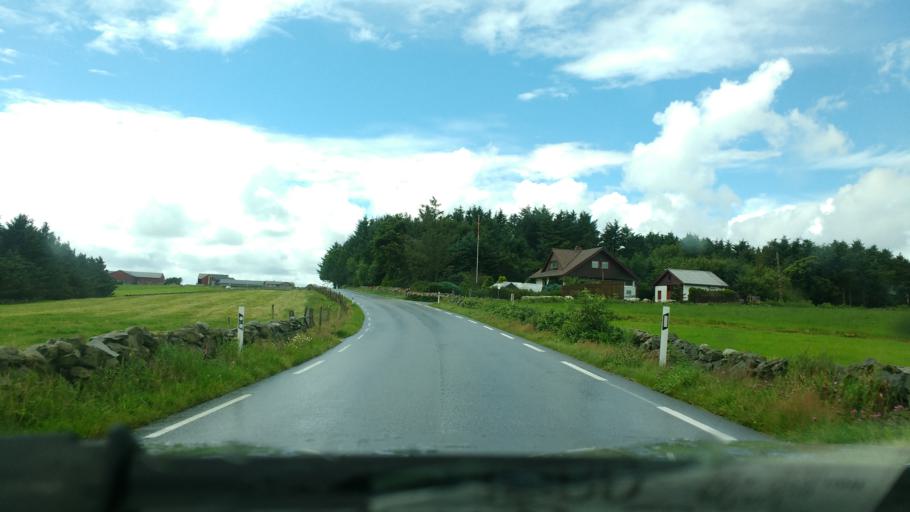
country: NO
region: Rogaland
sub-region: Klepp
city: Kleppe
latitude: 58.7812
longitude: 5.5503
